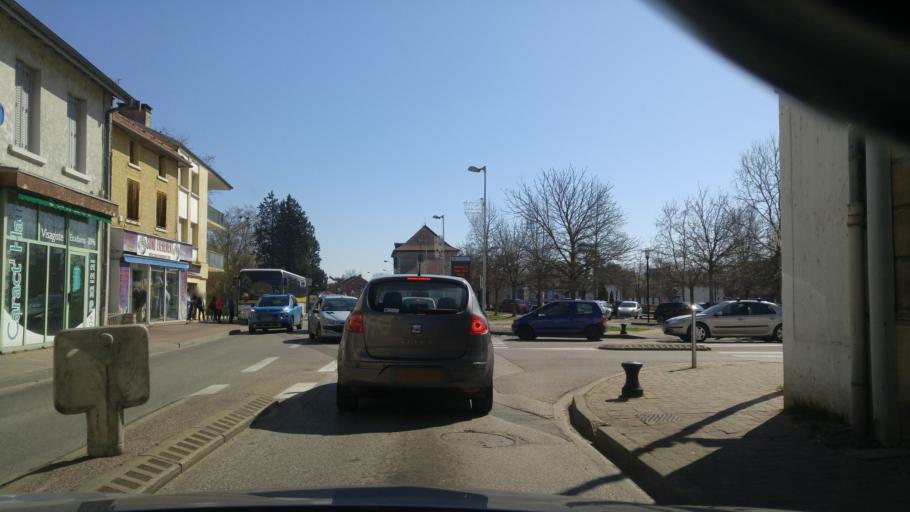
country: FR
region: Rhone-Alpes
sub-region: Departement de l'Isere
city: Pont-de-Cheruy
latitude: 45.7504
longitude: 5.1729
